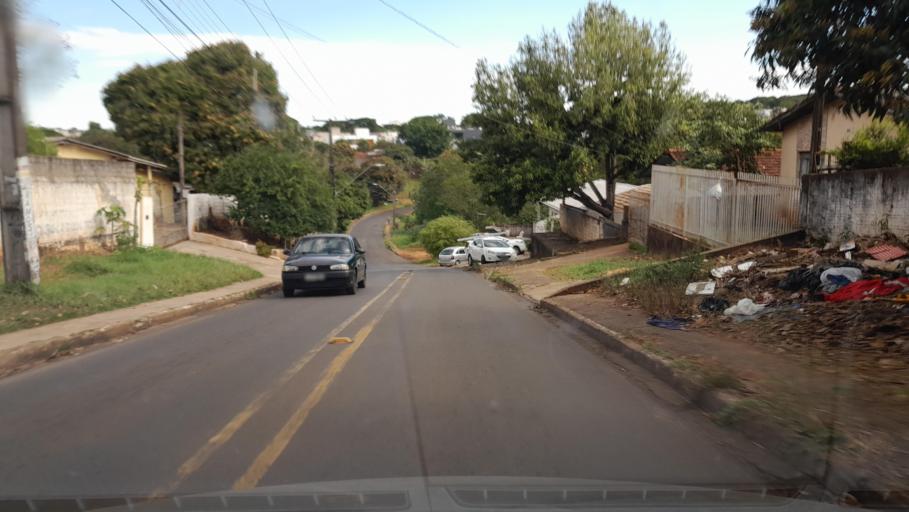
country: BR
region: Parana
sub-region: Umuarama
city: Umuarama
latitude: -23.7719
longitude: -53.3034
